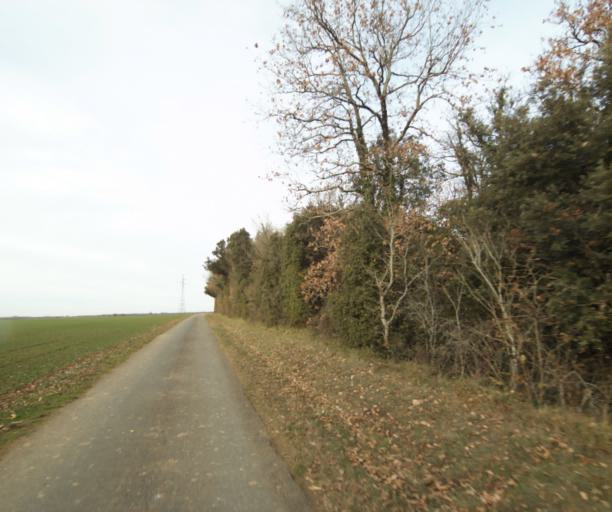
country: FR
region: Poitou-Charentes
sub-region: Departement de la Charente-Maritime
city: Saint-Hilaire-de-Villefranche
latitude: 45.8278
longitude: -0.5802
